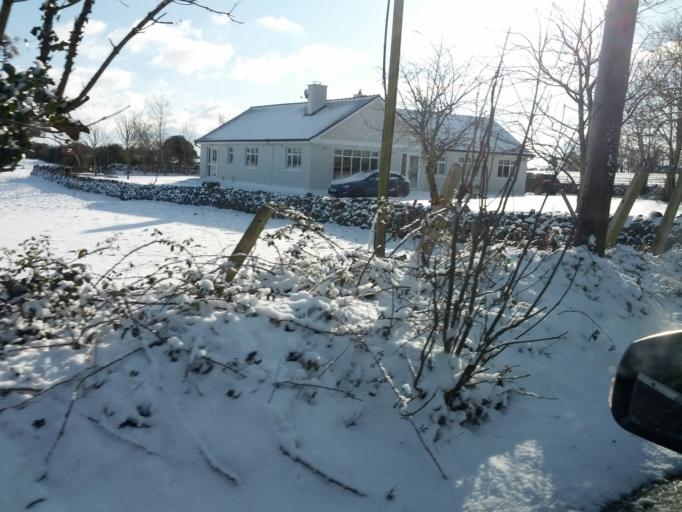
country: IE
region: Connaught
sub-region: County Galway
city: Athenry
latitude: 53.2045
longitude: -8.7827
